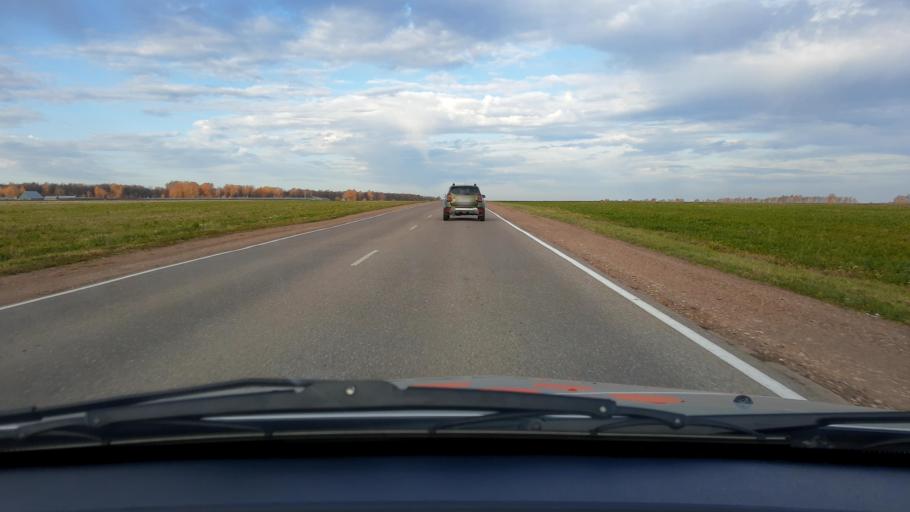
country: RU
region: Bashkortostan
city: Avdon
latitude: 54.8226
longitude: 55.6614
